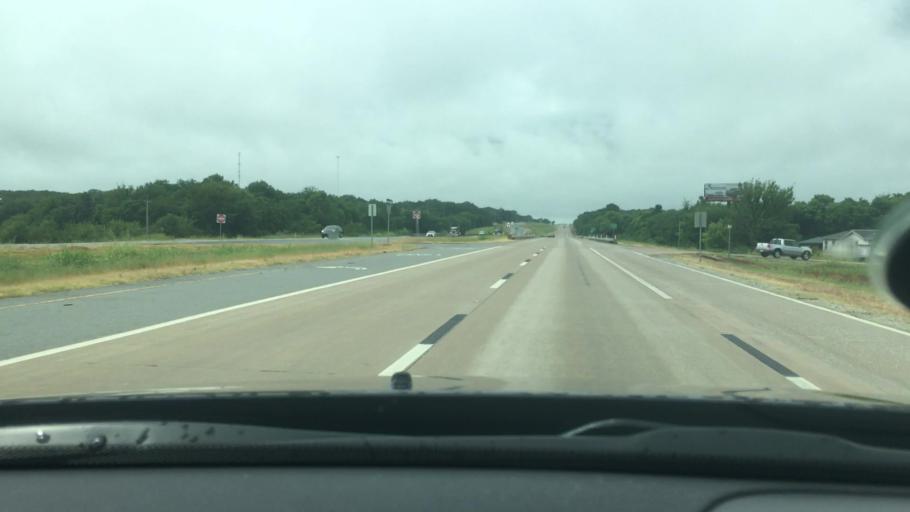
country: US
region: Oklahoma
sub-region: Atoka County
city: Atoka
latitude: 34.2450
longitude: -96.2178
